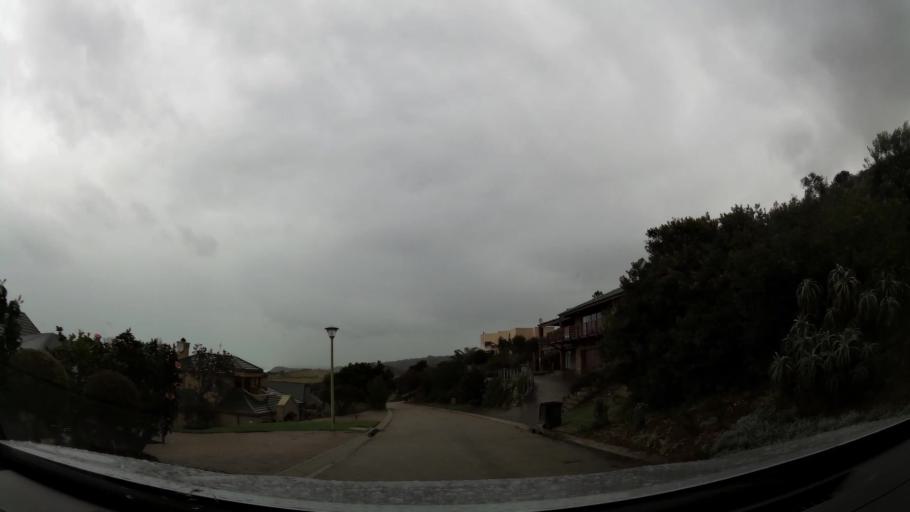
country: ZA
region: Western Cape
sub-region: Eden District Municipality
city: George
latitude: -34.0461
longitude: 22.2855
